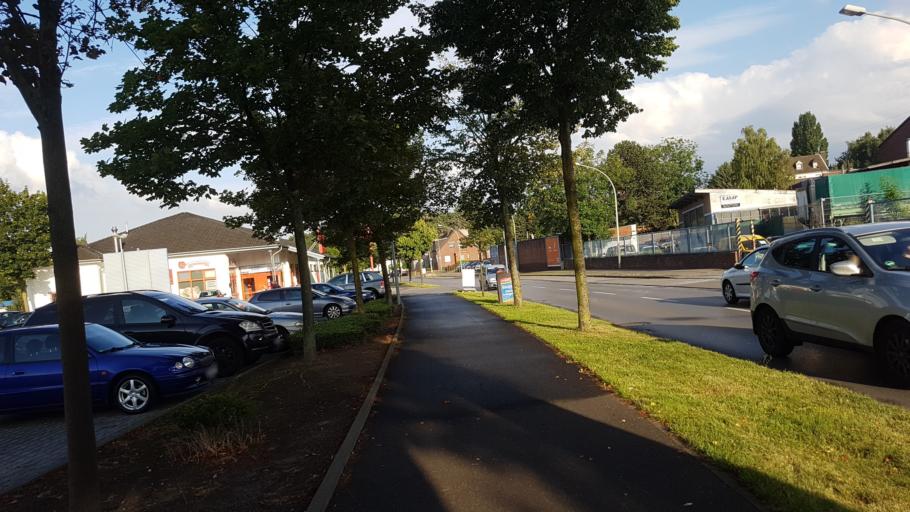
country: DE
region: North Rhine-Westphalia
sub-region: Regierungsbezirk Koln
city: Eschweiler
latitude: 50.8125
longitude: 6.2705
